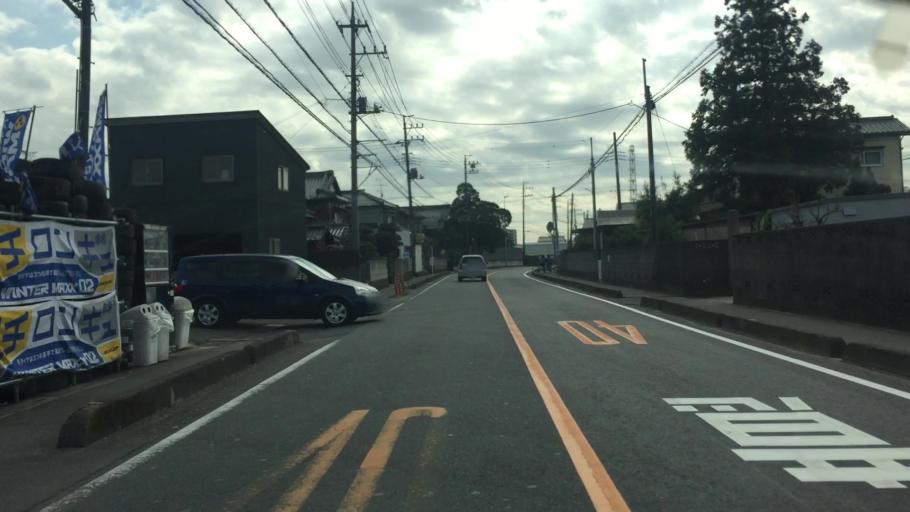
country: JP
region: Saitama
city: Yoshikawa
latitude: 35.8703
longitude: 139.8647
